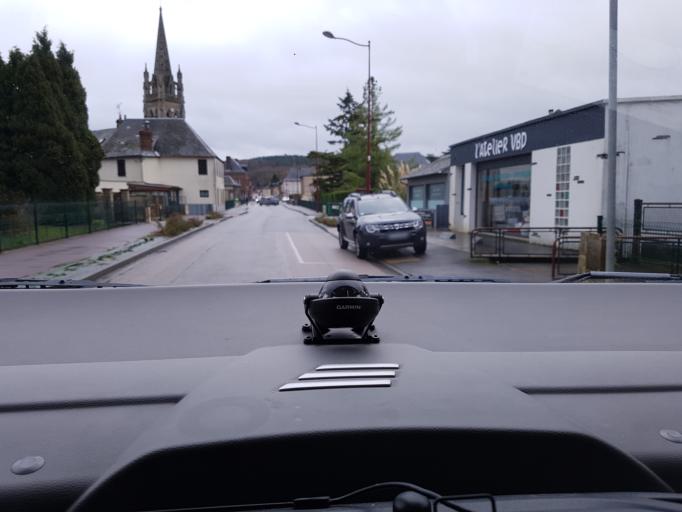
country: FR
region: Haute-Normandie
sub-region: Departement de l'Eure
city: Pont-Saint-Pierre
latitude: 49.3345
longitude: 1.2730
